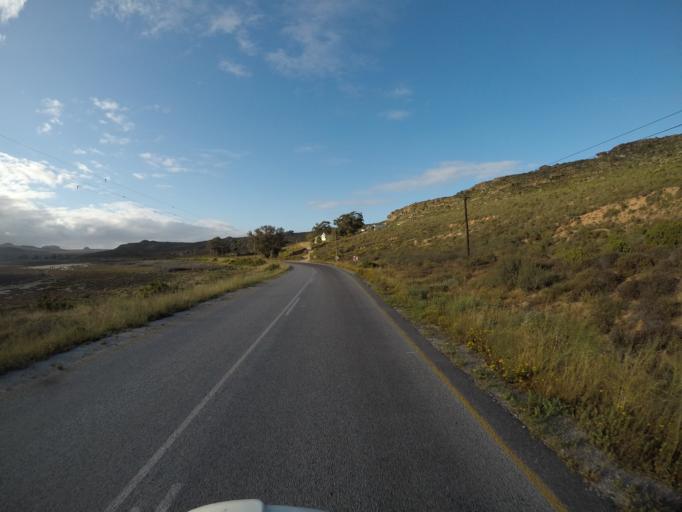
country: ZA
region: Western Cape
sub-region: West Coast District Municipality
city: Clanwilliam
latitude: -32.3199
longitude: 18.3577
